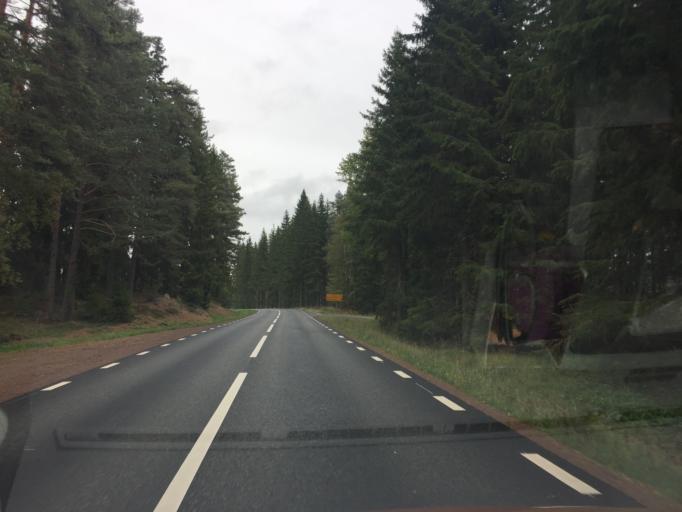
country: SE
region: Joenkoeping
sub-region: Aneby Kommun
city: Hestra
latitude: 57.8944
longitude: 14.5499
